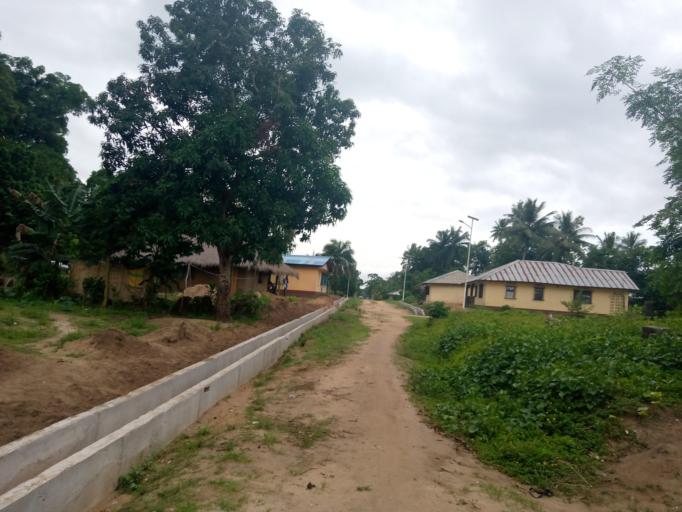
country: SL
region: Southern Province
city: Bonthe
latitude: 7.5226
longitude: -12.5067
